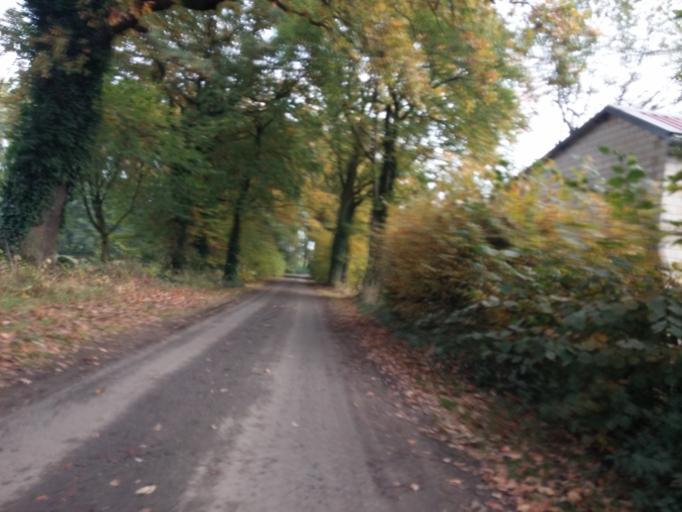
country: DE
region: North Rhine-Westphalia
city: Dorsten
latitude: 51.6326
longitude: 6.9820
